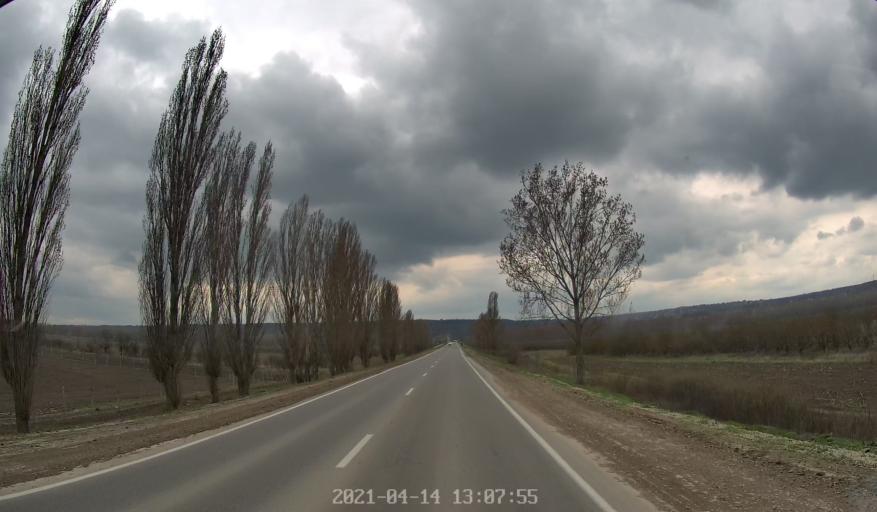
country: MD
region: Chisinau
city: Vadul lui Voda
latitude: 47.0970
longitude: 29.0961
